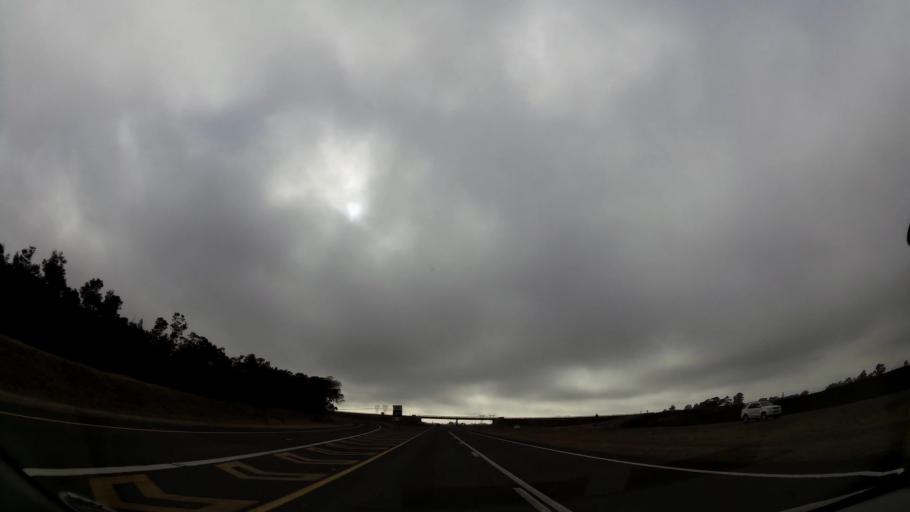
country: ZA
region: Mpumalanga
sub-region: Nkangala District Municipality
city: Delmas
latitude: -26.0580
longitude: 28.8068
